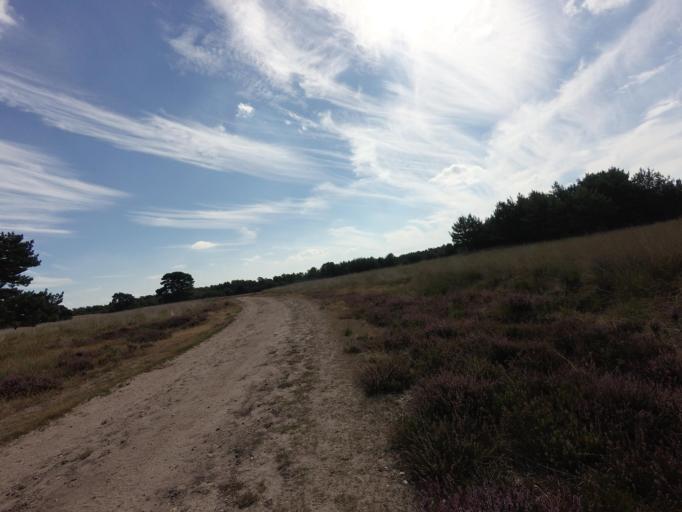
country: NL
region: Gelderland
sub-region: Gemeente Rheden
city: Rheden
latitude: 52.0456
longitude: 6.0024
